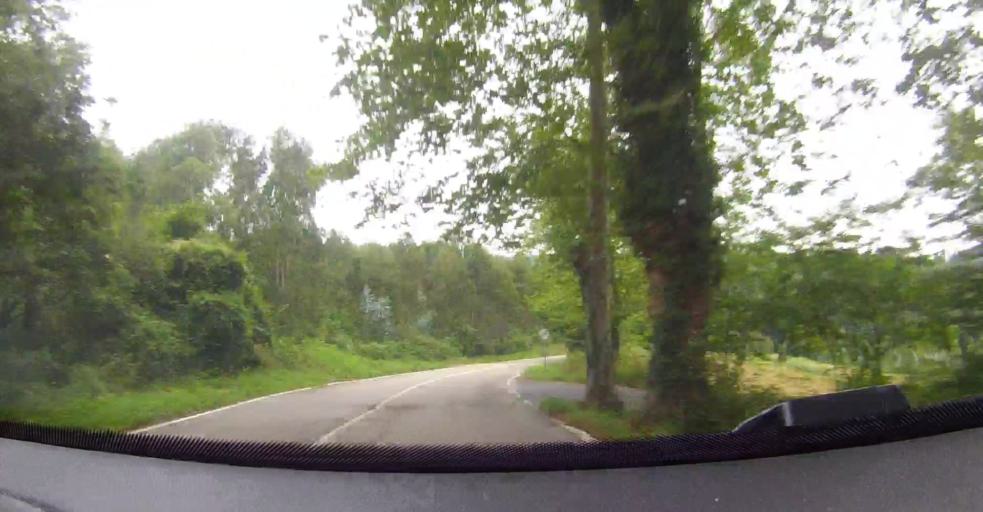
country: ES
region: Basque Country
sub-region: Bizkaia
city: Balmaseda
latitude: 43.2393
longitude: -3.2869
